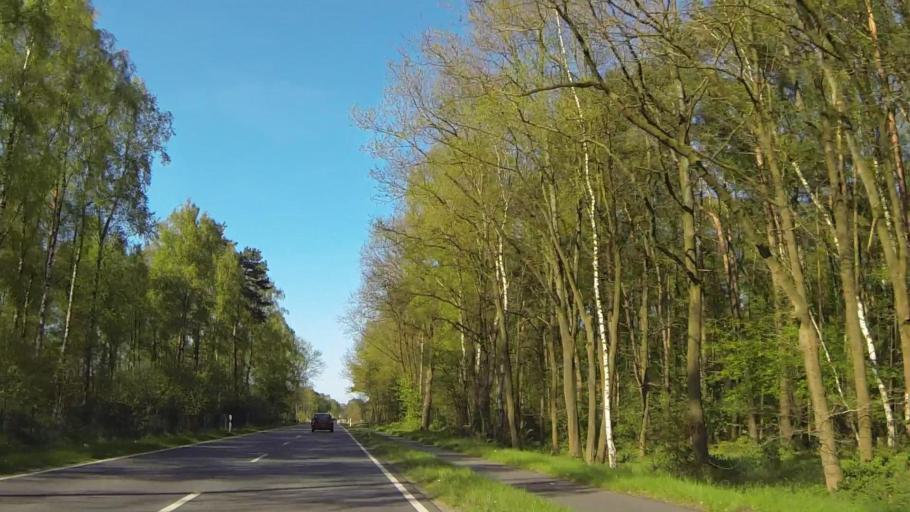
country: DE
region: Schleswig-Holstein
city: Appen
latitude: 53.6215
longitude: 9.7276
